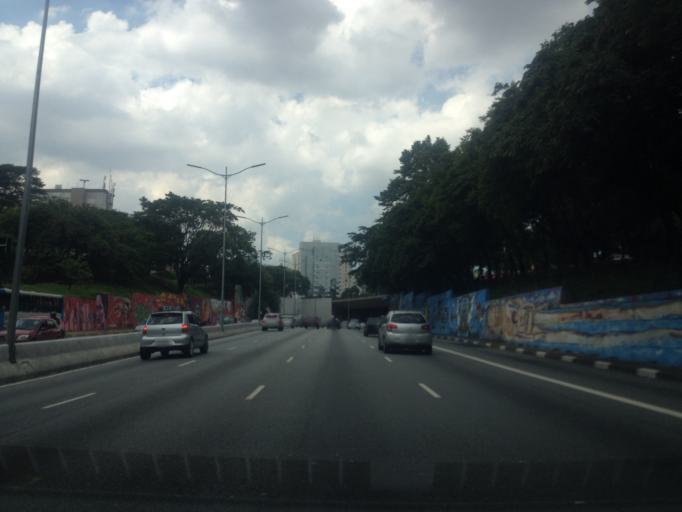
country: BR
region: Sao Paulo
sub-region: Sao Paulo
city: Sao Paulo
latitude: -23.5733
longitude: -46.6412
